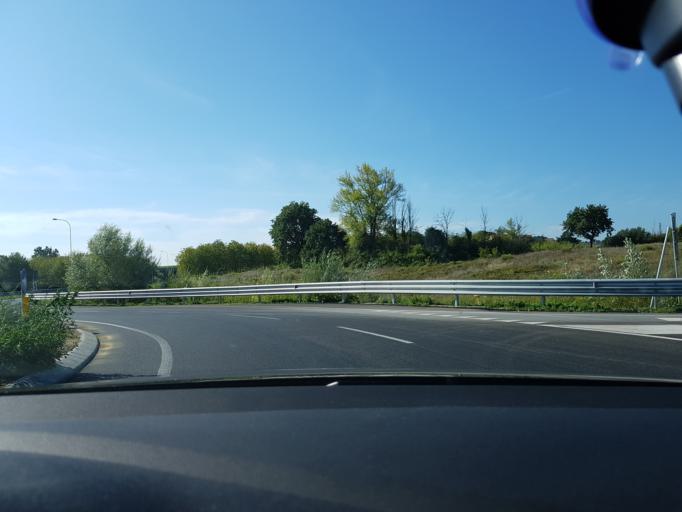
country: IT
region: Tuscany
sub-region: Province of Pisa
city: Ponte A Elsa
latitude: 43.6951
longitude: 10.9108
